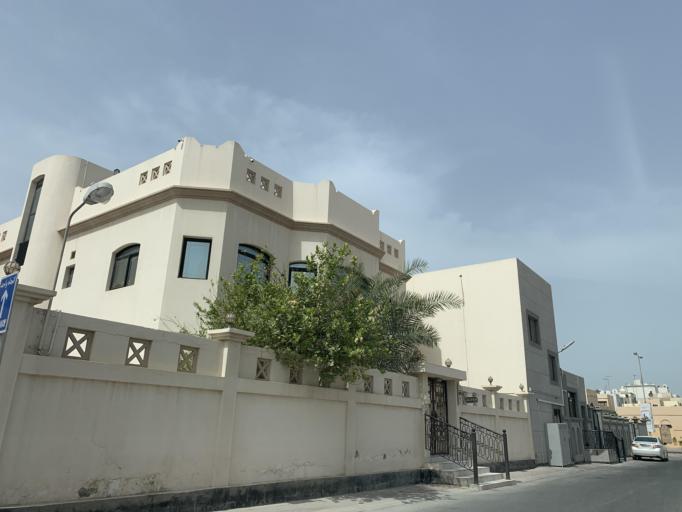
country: BH
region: Northern
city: Ar Rifa'
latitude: 26.1305
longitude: 50.5618
